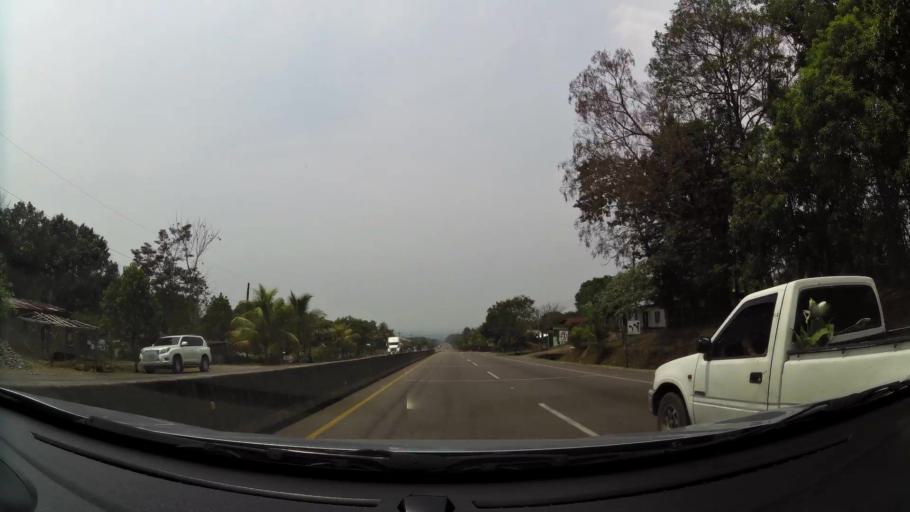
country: HN
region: Cortes
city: Oropendolas
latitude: 15.0129
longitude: -87.9273
